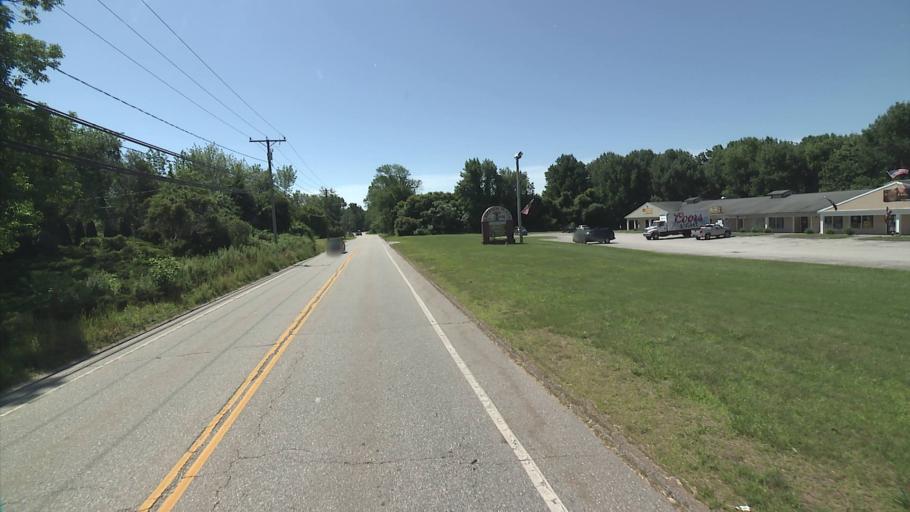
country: US
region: Connecticut
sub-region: Windham County
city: Willimantic
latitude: 41.6797
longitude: -72.2360
